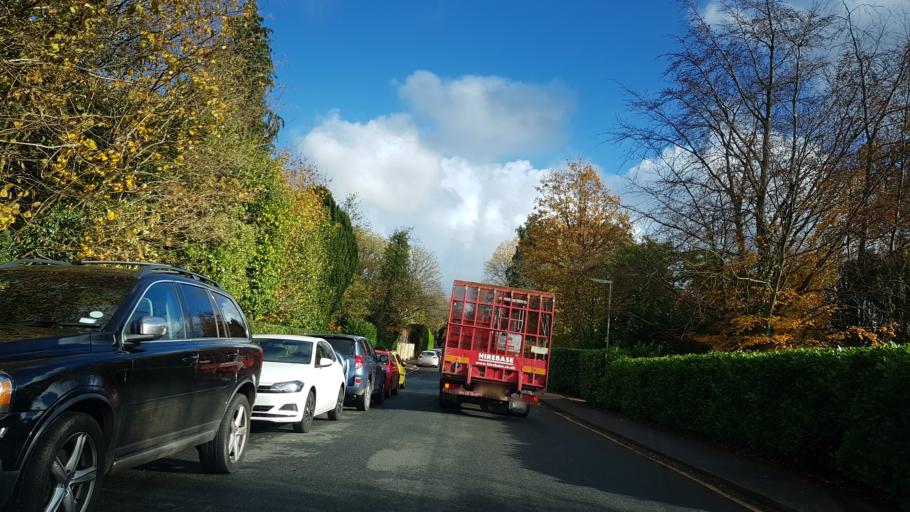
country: GB
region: England
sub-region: Surrey
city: Haslemere
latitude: 51.0913
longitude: -0.7172
